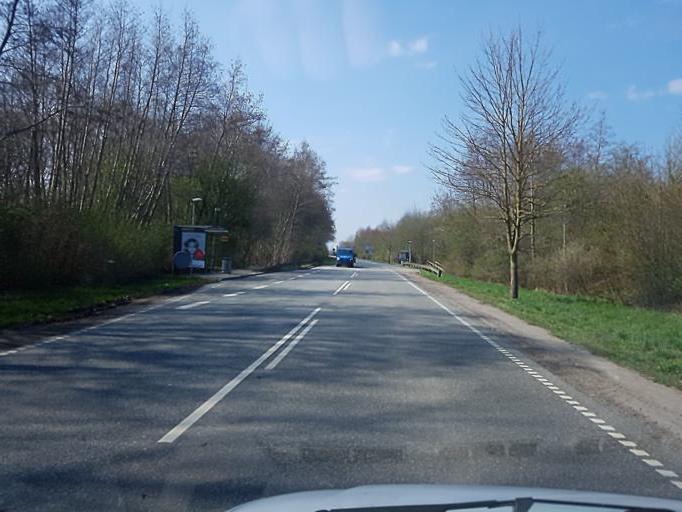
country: DK
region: South Denmark
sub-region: Odense Kommune
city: Neder Holluf
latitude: 55.3599
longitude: 10.4722
